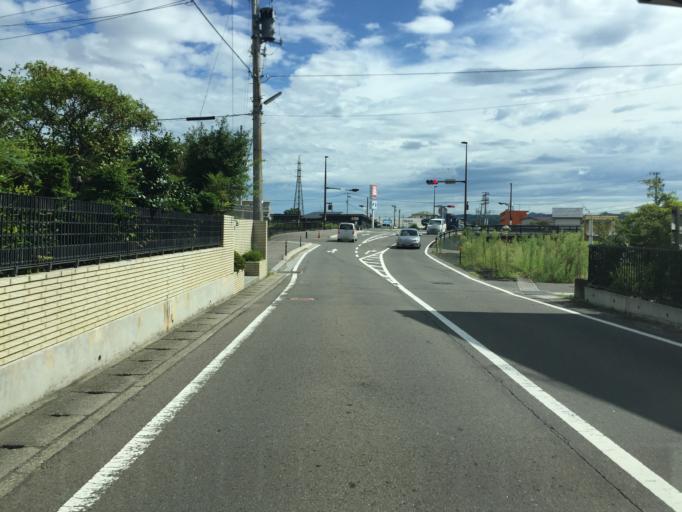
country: JP
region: Fukushima
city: Fukushima-shi
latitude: 37.7306
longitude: 140.4414
